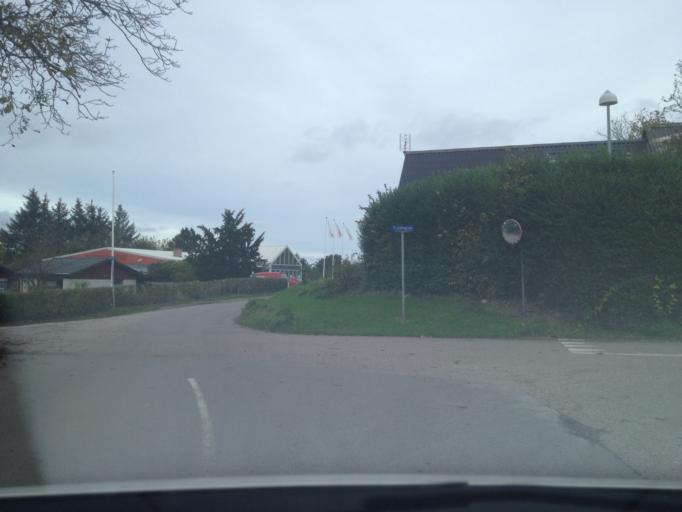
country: DK
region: Zealand
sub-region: Odsherred Kommune
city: Hojby
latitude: 55.9328
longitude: 11.6055
